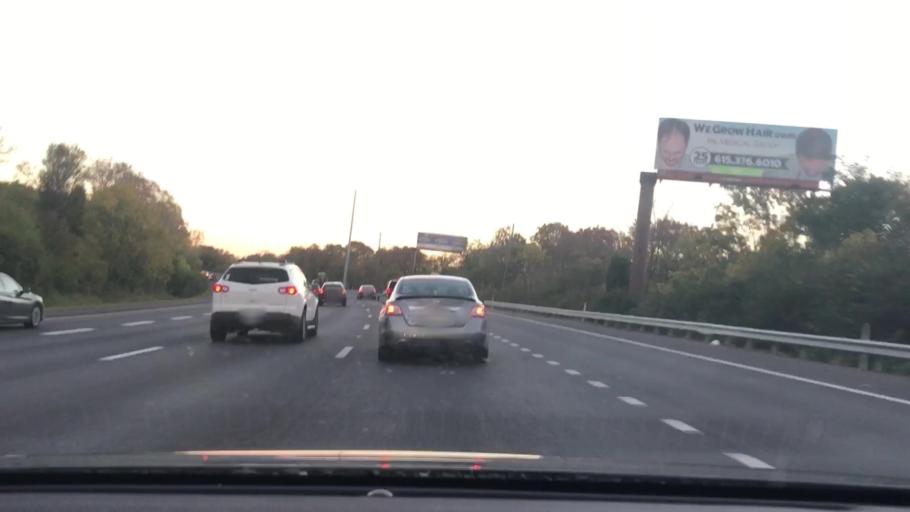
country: US
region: Tennessee
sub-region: Williamson County
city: Brentwood
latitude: 36.0465
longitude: -86.7770
